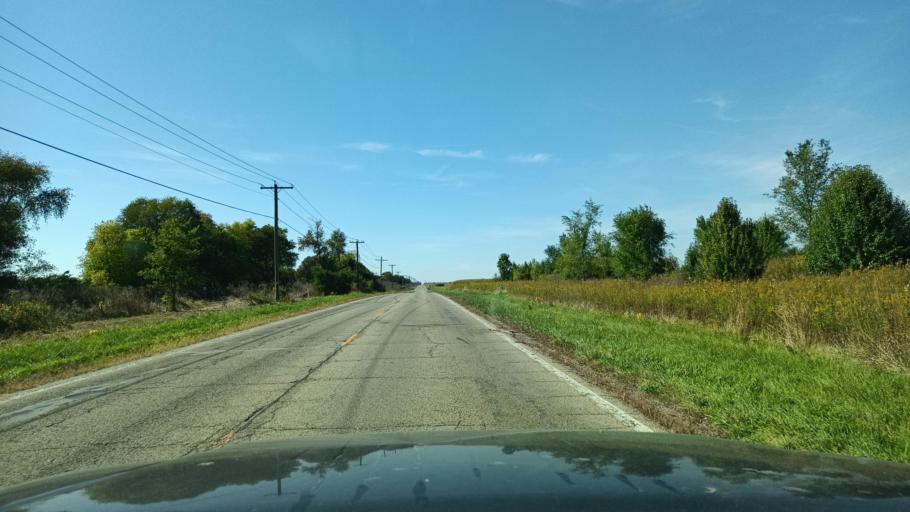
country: US
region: Illinois
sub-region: Champaign County
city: Mahomet
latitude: 40.1973
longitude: -88.4343
